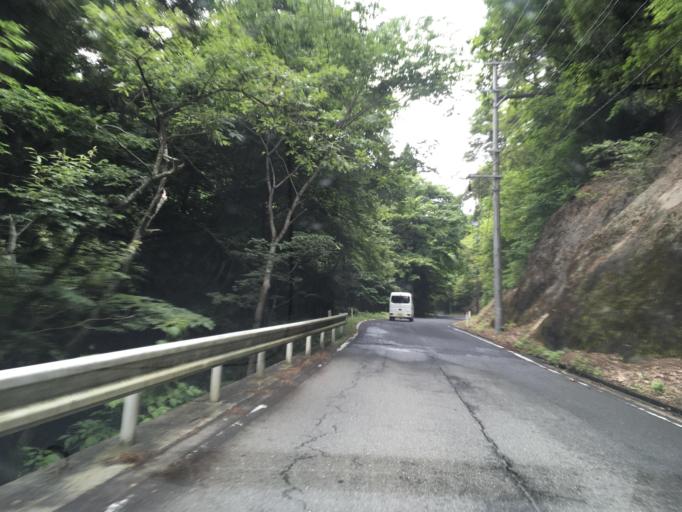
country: JP
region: Iwate
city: Ofunato
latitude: 38.9113
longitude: 141.6194
